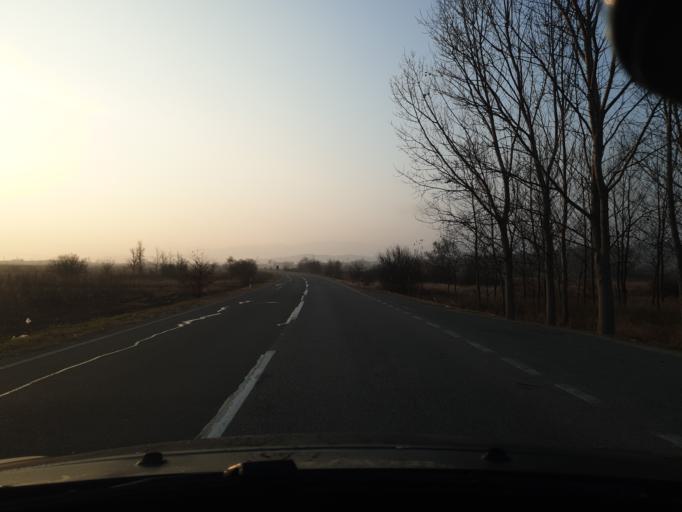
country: RS
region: Central Serbia
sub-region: Jablanicki Okrug
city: Leskovac
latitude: 42.9468
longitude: 21.9919
